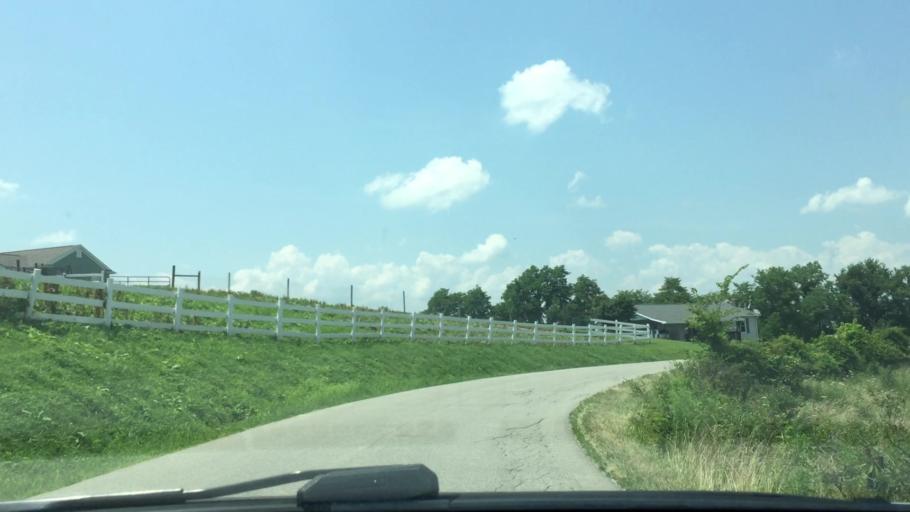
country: US
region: West Virginia
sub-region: Wetzel County
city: New Martinsville
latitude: 39.7169
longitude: -80.7482
